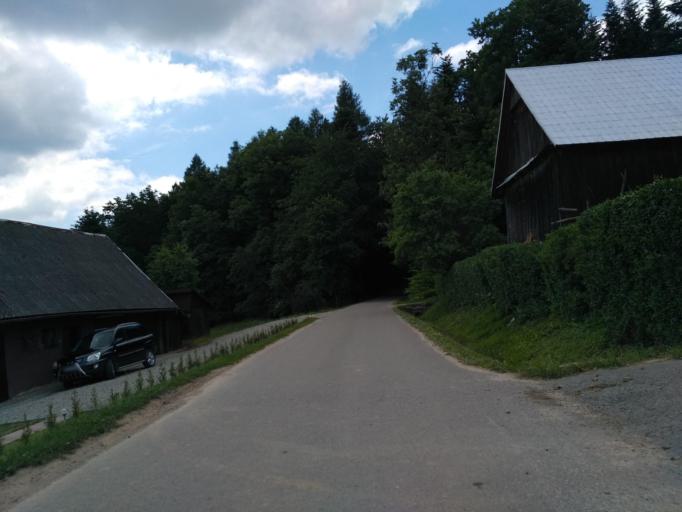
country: PL
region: Subcarpathian Voivodeship
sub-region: Powiat brzozowski
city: Wesola
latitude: 49.7595
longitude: 22.1299
